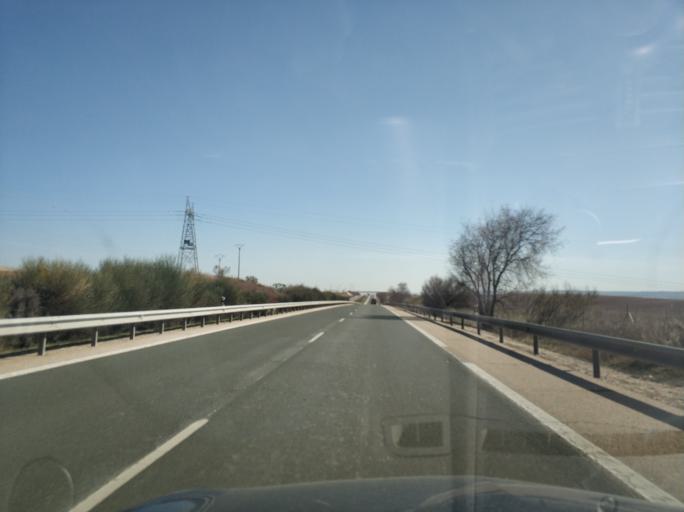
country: ES
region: Castille and Leon
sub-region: Provincia de Valladolid
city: Cisterniga
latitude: 41.5971
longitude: -4.6472
